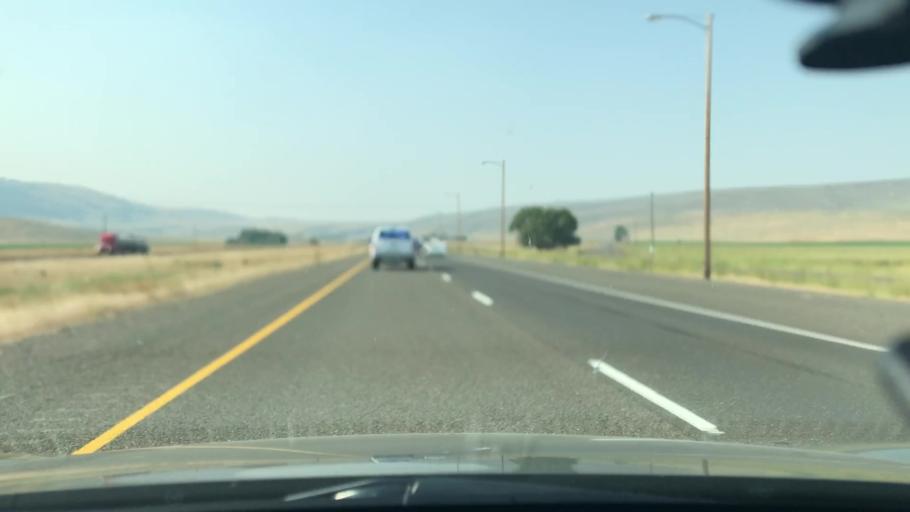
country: US
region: Oregon
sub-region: Union County
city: Union
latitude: 45.1110
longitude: -117.9578
